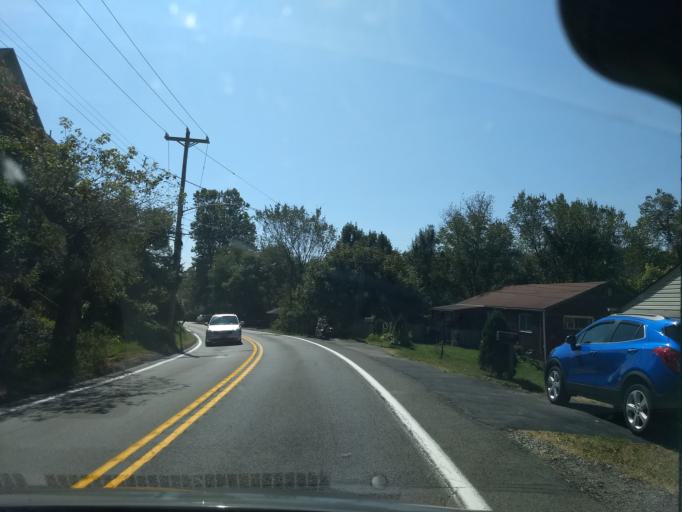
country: US
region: Pennsylvania
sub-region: Allegheny County
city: North Versailles
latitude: 40.3687
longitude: -79.8292
